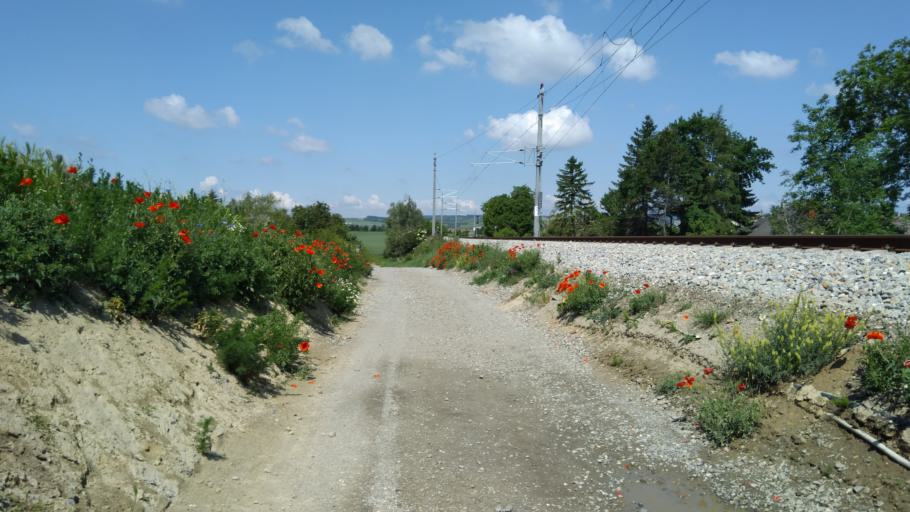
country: AT
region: Lower Austria
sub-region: Politischer Bezirk Mistelbach
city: Wolkersdorf im Weinviertel
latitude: 48.3830
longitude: 16.5086
